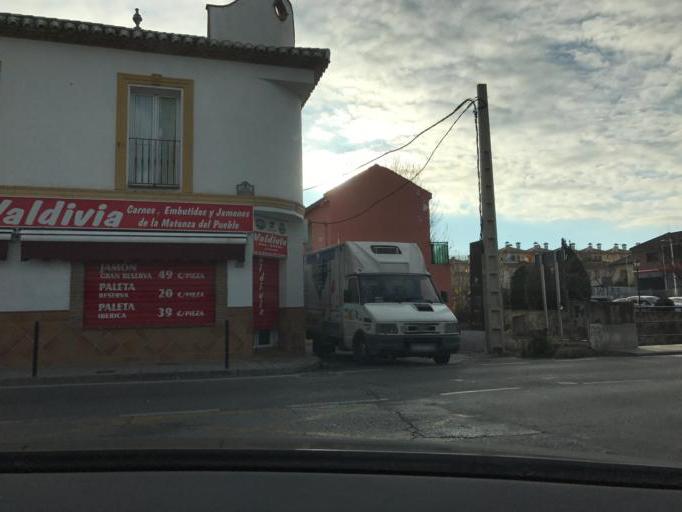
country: ES
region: Andalusia
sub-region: Provincia de Granada
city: Huetor Vega
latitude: 37.1404
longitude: -3.5699
